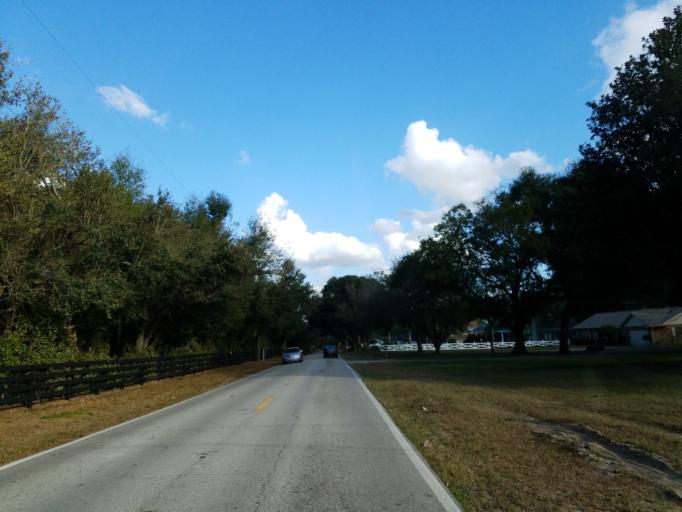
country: US
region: Florida
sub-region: Hillsborough County
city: Brandon
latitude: 27.9524
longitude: -82.3083
